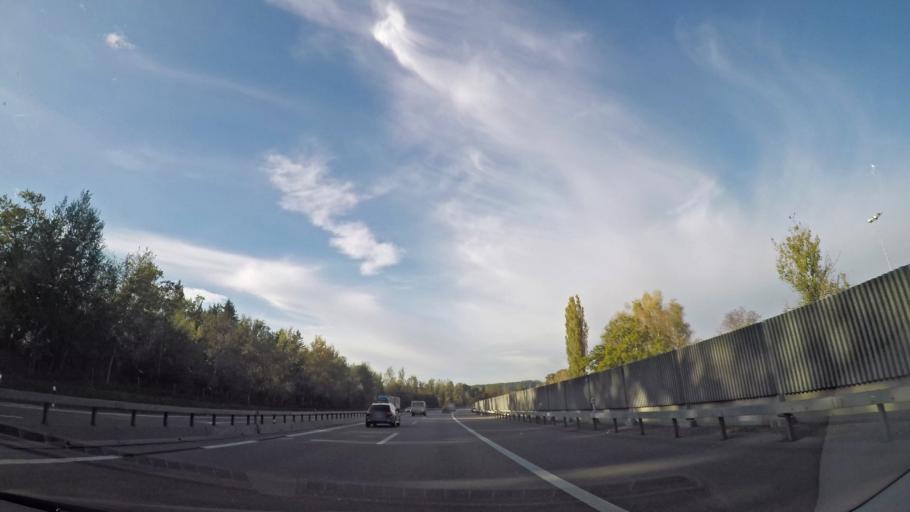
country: CH
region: Bern
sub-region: Bern-Mittelland District
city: Rubigen
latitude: 46.8936
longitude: 7.5361
